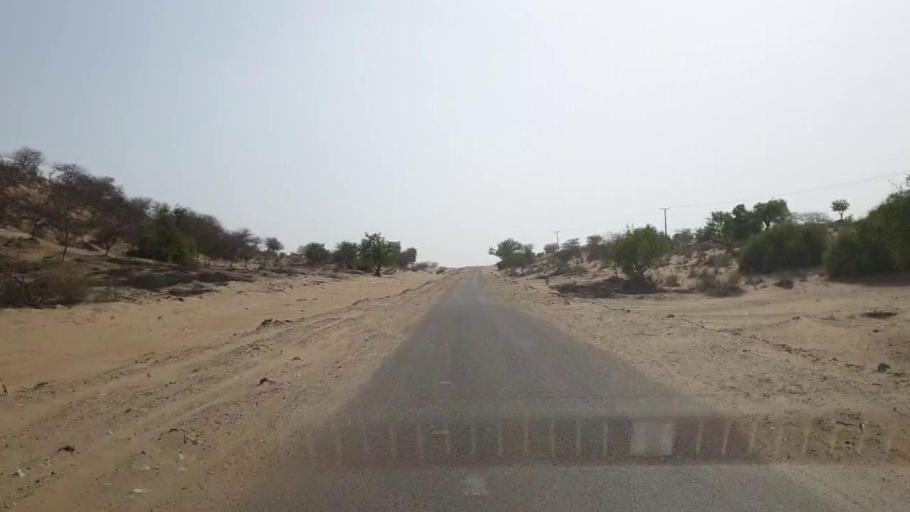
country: PK
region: Sindh
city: Mithi
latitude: 24.6213
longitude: 69.8997
